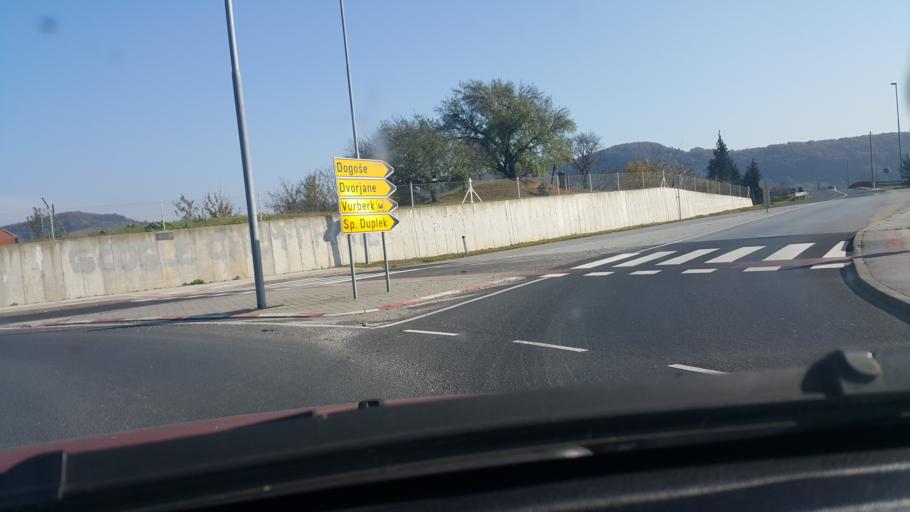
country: SI
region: Miklavz na Dravskem Polju
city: Miklavz na Dravskem Polju
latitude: 46.5262
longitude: 15.7006
